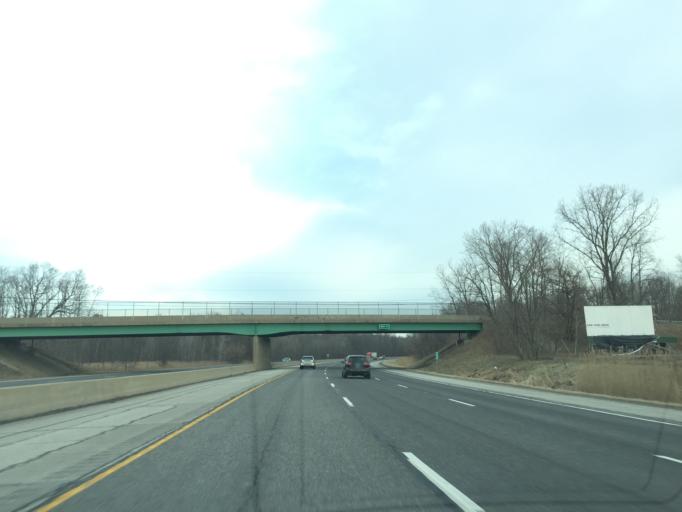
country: US
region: Indiana
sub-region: LaPorte County
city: Long Beach
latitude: 41.7228
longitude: -86.8056
